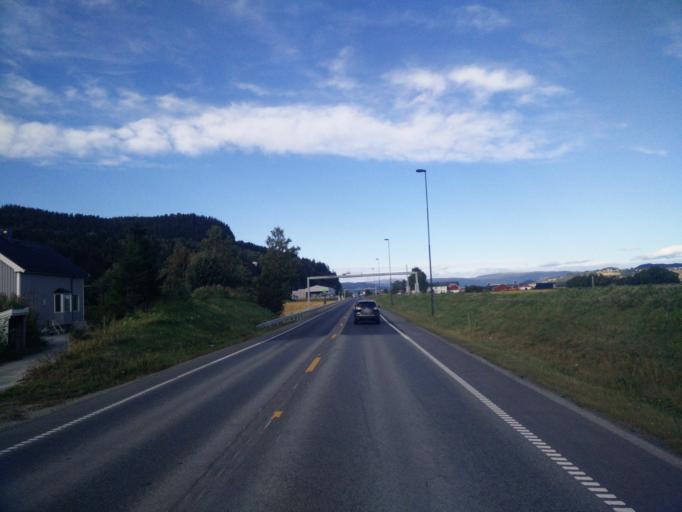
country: NO
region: Sor-Trondelag
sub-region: Melhus
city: Melhus
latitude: 63.3231
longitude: 10.2504
